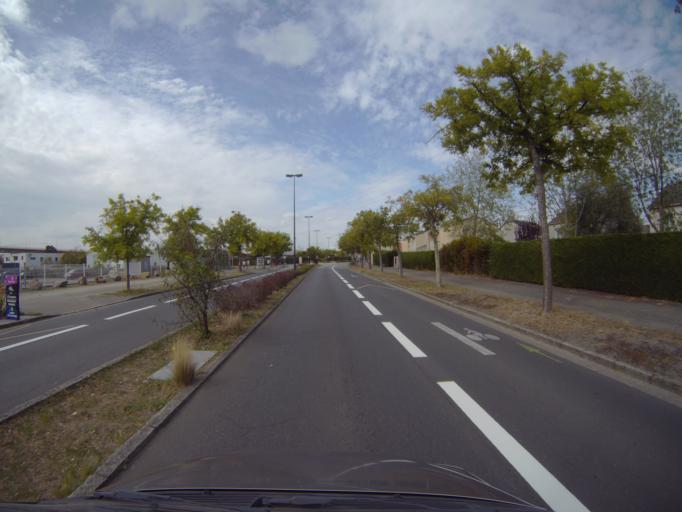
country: FR
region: Pays de la Loire
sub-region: Departement de la Loire-Atlantique
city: Bouguenais
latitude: 47.1994
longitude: -1.6105
